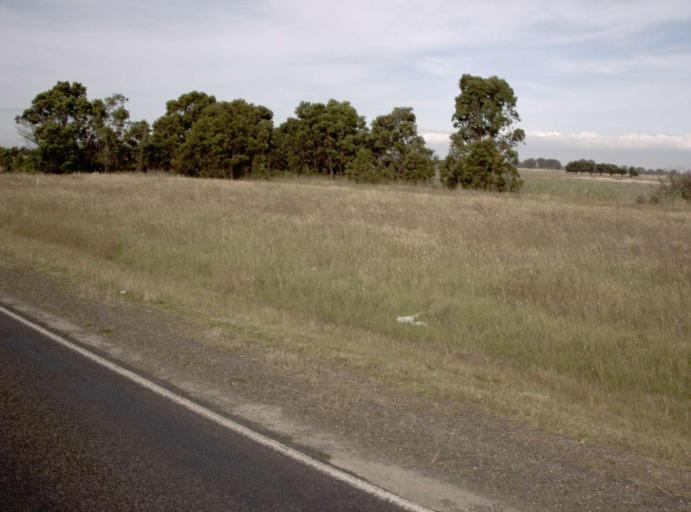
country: AU
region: Victoria
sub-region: Latrobe
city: Traralgon
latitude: -38.0820
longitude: 146.6072
